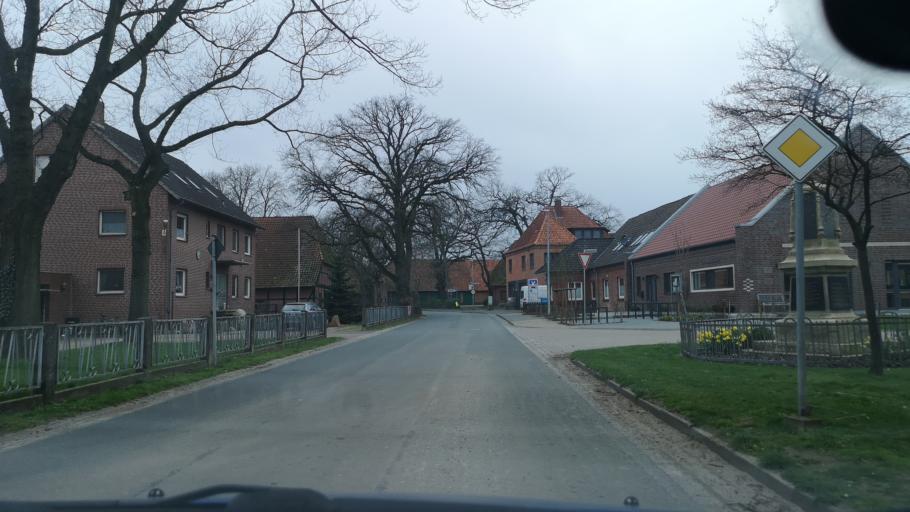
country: DE
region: Lower Saxony
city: Neustadt am Rubenberge
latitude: 52.5463
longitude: 9.4149
